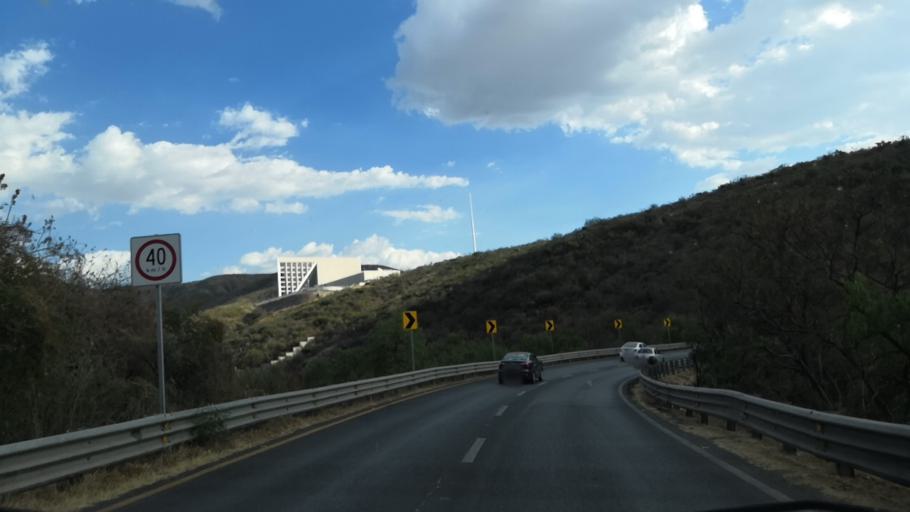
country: MX
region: Guanajuato
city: Marfil
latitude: 21.0021
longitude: -101.2818
